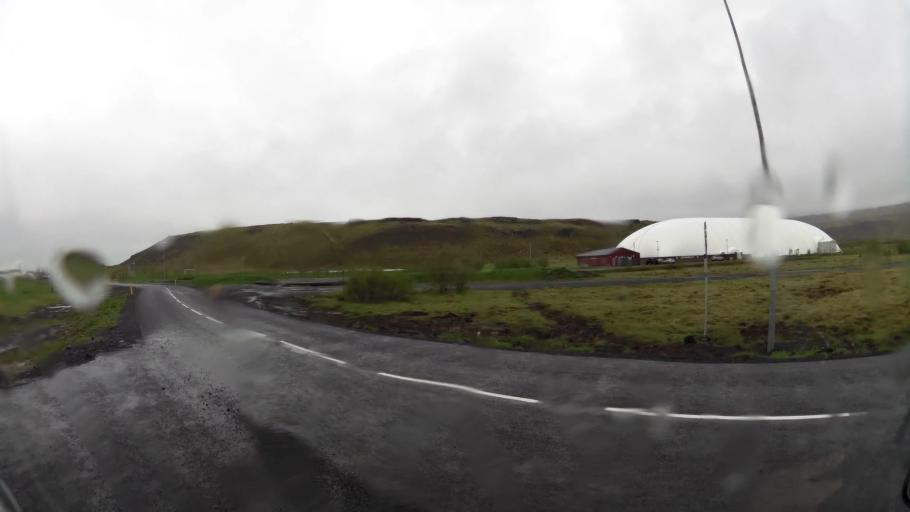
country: IS
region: South
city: Hveragerdi
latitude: 64.0116
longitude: -21.1915
